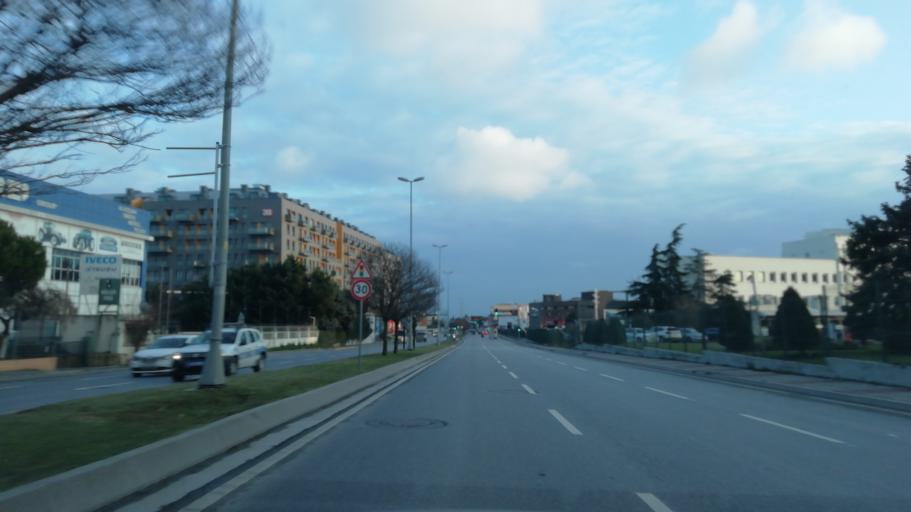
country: TR
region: Istanbul
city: Yakuplu
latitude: 40.9938
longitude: 28.7166
